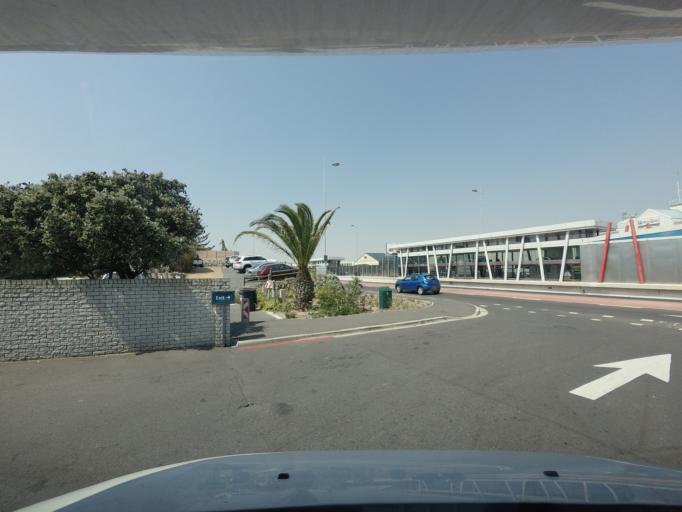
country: ZA
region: Western Cape
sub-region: City of Cape Town
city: Sunset Beach
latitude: -33.7306
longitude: 18.4423
